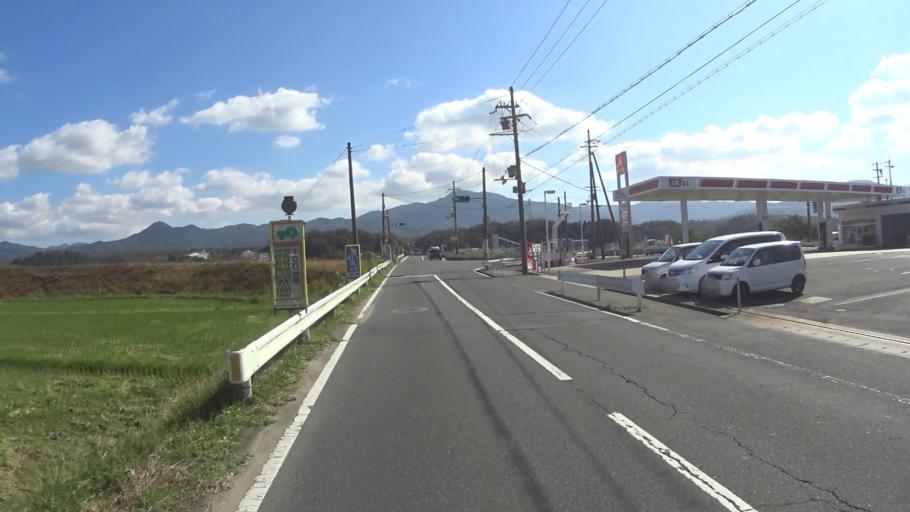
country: JP
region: Kyoto
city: Miyazu
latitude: 35.6701
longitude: 135.0862
